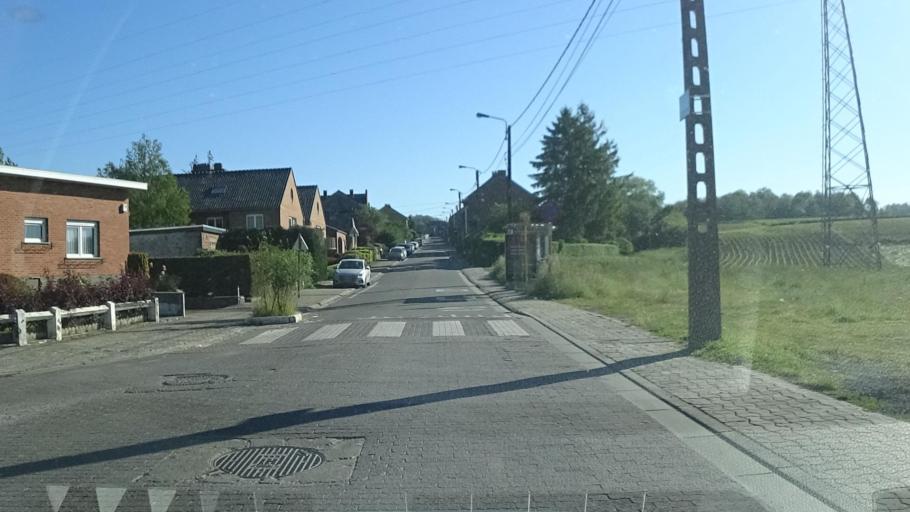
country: BE
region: Wallonia
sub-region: Province du Hainaut
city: La Louviere
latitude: 50.4589
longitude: 4.1735
